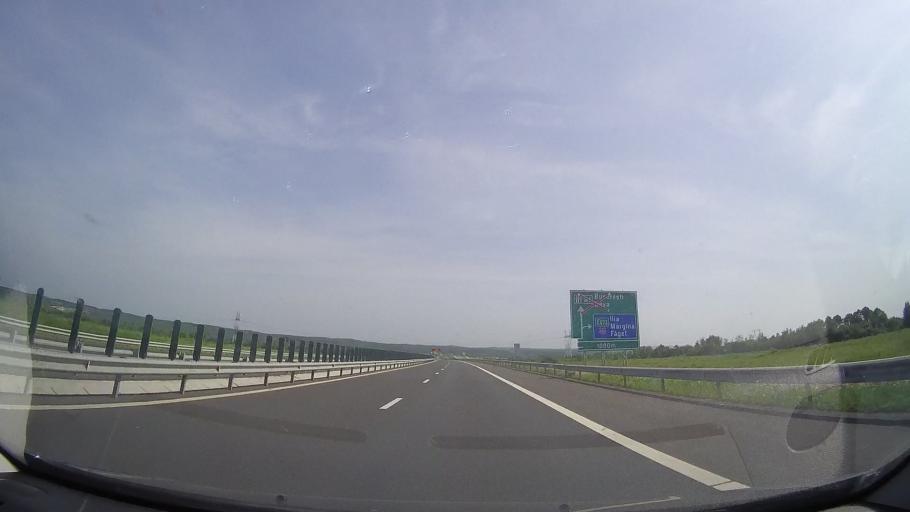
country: RO
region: Timis
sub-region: Comuna Margina
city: Margina
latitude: 45.8488
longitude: 22.2362
